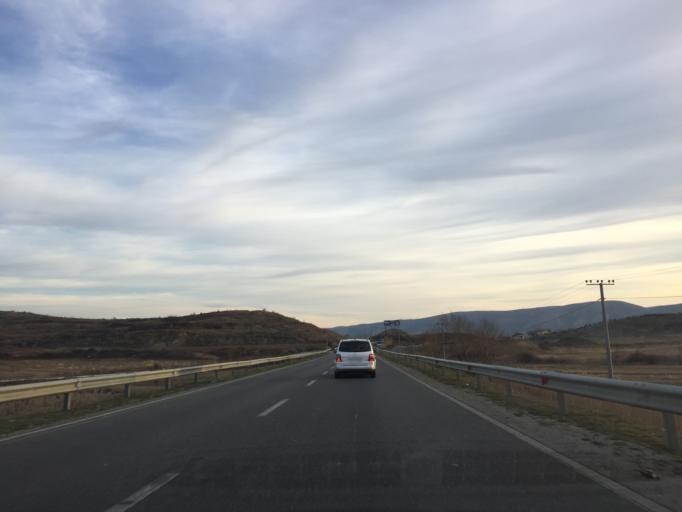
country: AL
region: Shkoder
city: Vukatane
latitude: 41.9608
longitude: 19.5523
